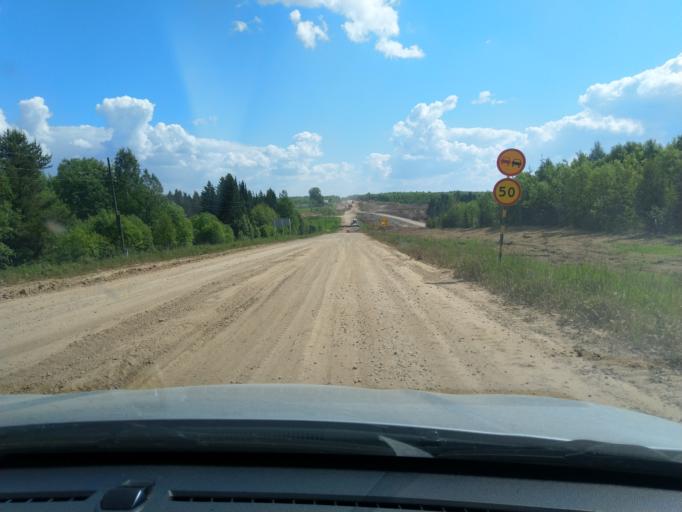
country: RU
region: Perm
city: Pozhva
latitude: 59.4234
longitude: 56.1335
